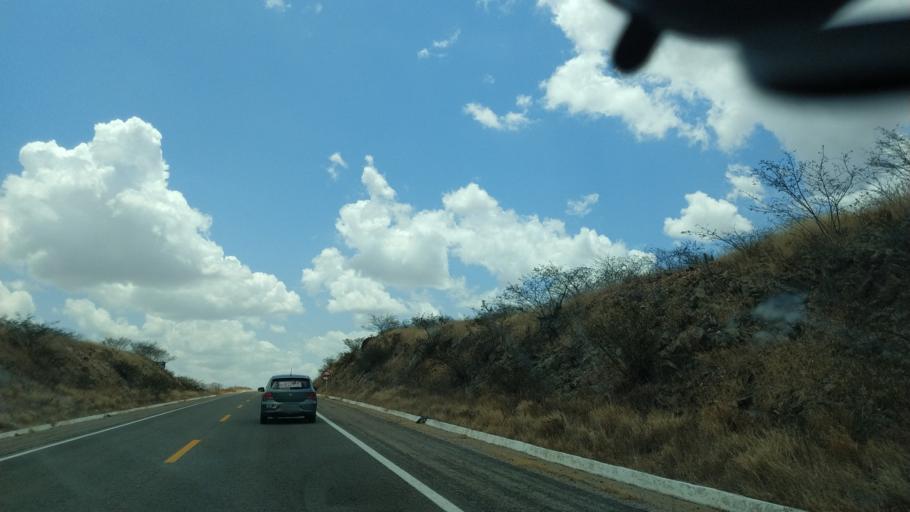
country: BR
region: Rio Grande do Norte
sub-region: Cerro Cora
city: Cerro Cora
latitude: -6.2007
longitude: -36.3371
